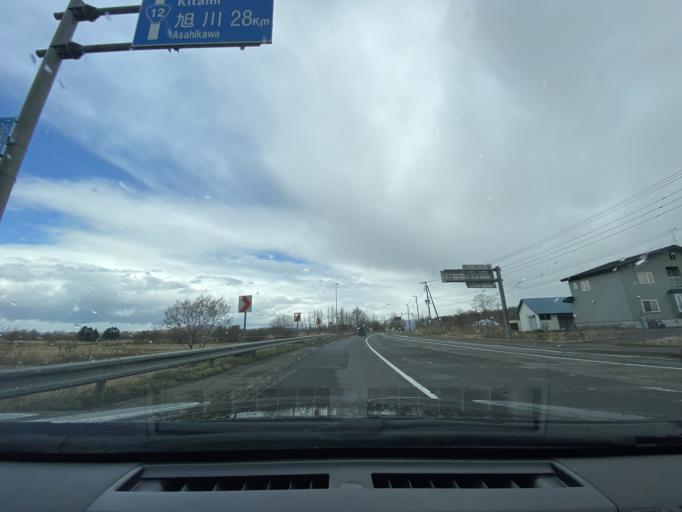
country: JP
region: Hokkaido
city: Fukagawa
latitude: 43.7005
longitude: 142.0729
